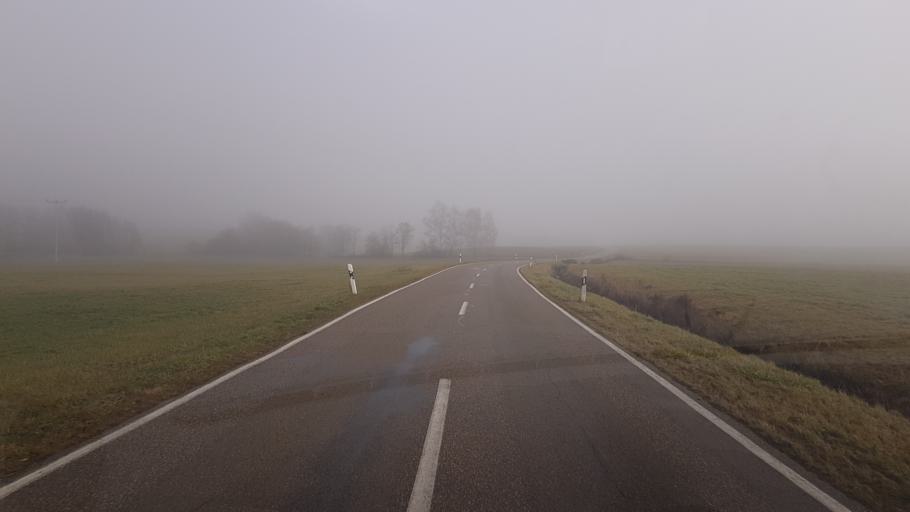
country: DE
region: Bavaria
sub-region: Regierungsbezirk Mittelfranken
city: Wettringen
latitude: 49.2417
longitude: 10.1801
